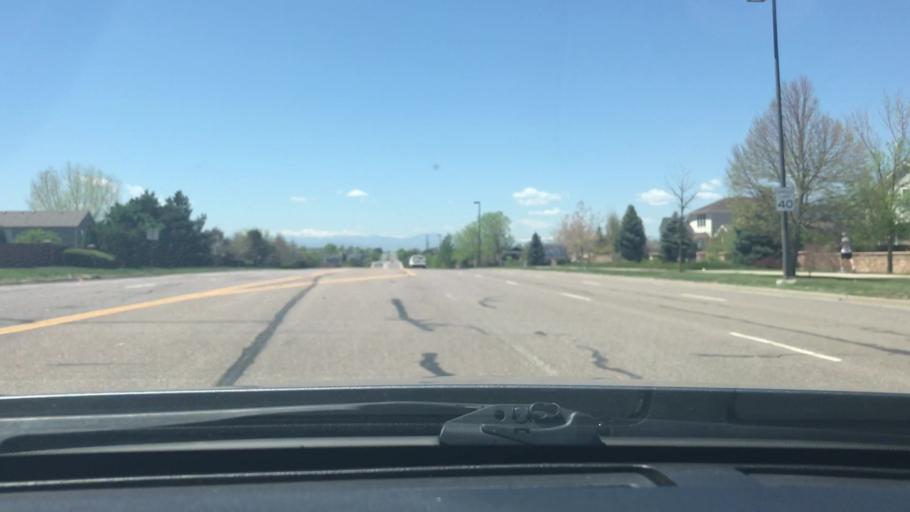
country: US
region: Colorado
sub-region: Arapahoe County
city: Dove Valley
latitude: 39.6530
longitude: -104.7444
